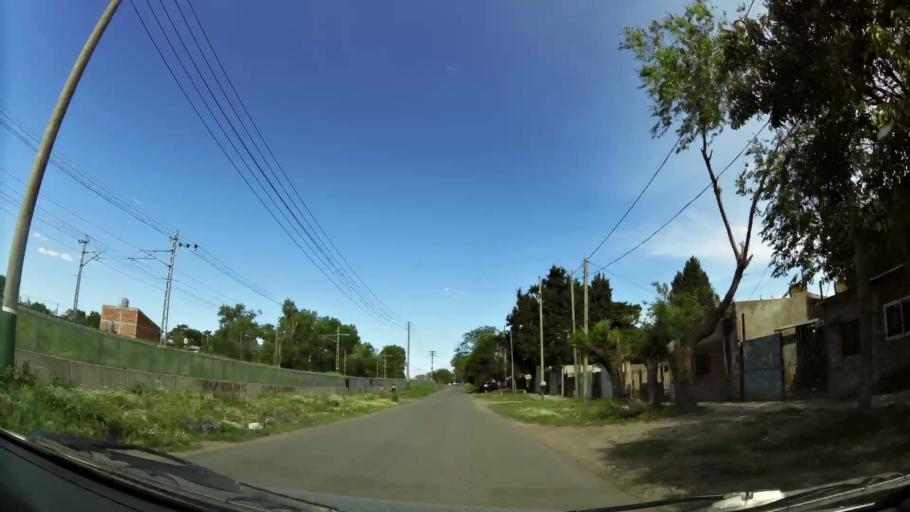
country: AR
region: Buenos Aires
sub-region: Partido de Almirante Brown
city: Adrogue
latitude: -34.8000
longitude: -58.3452
